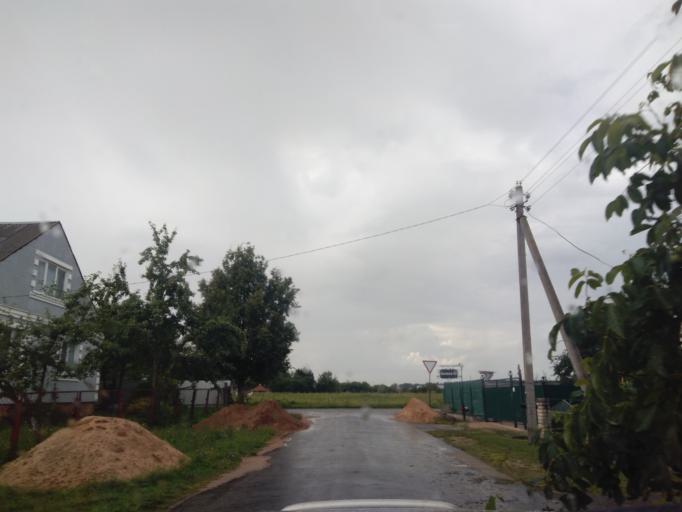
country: BY
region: Minsk
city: Kapyl'
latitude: 53.1653
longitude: 27.0852
